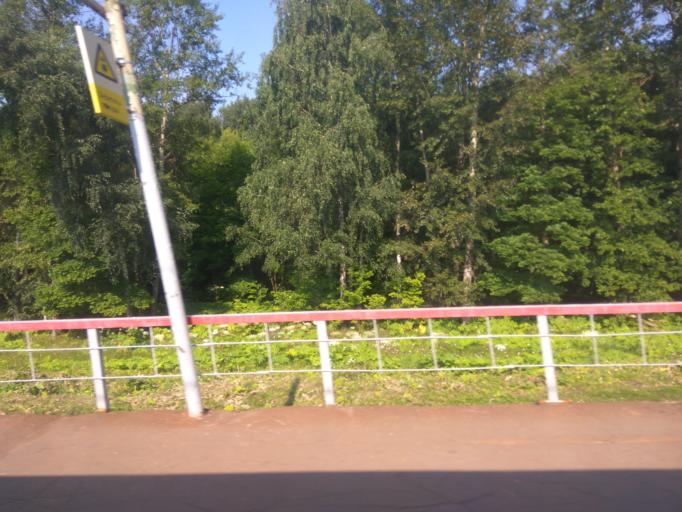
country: RU
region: Moscow
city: Annino
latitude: 55.5723
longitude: 37.6121
